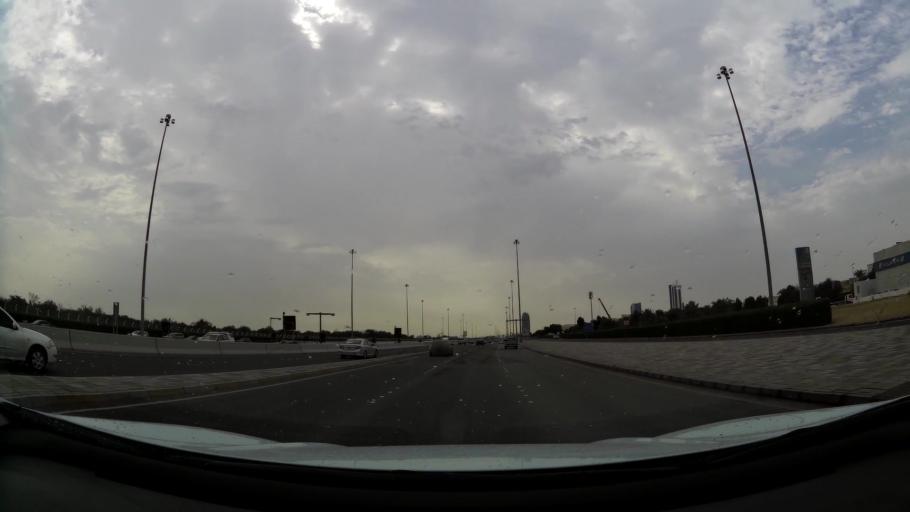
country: AE
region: Abu Dhabi
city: Abu Dhabi
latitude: 24.4767
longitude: 54.3891
